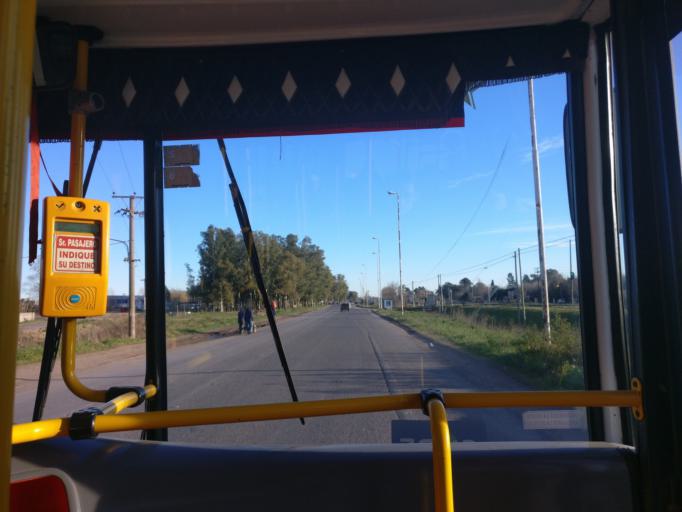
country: AR
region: Buenos Aires
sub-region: Partido de Ezeiza
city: Ezeiza
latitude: -34.9334
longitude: -58.6177
